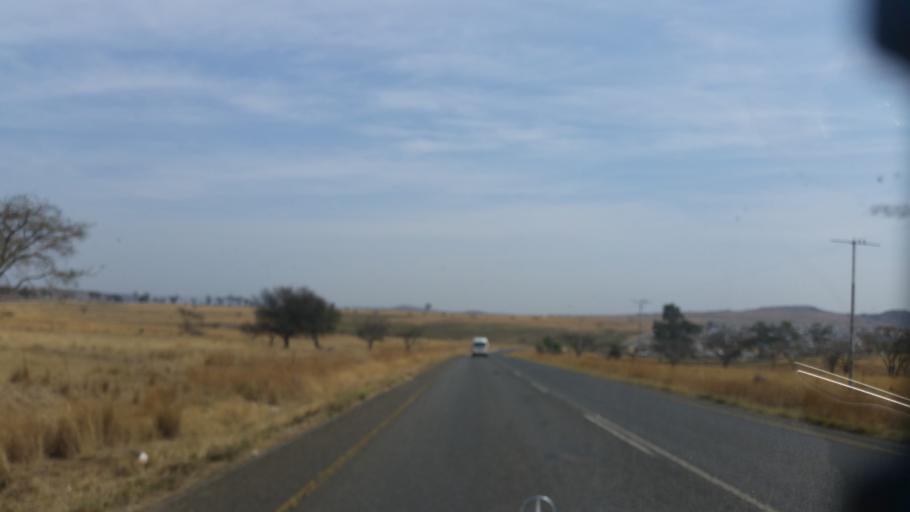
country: ZA
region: KwaZulu-Natal
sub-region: uThukela District Municipality
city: Estcourt
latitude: -29.0533
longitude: 29.9224
